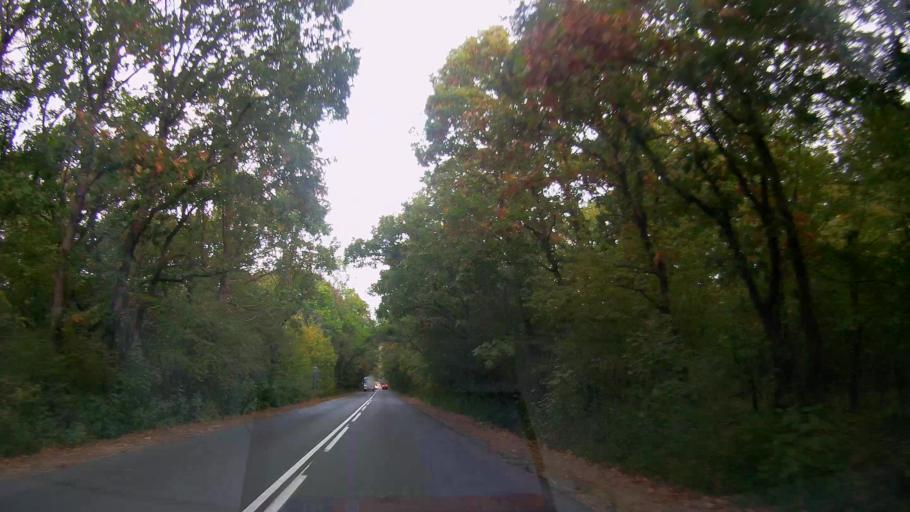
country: BG
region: Burgas
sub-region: Obshtina Primorsko
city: Primorsko
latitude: 42.2963
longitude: 27.7298
